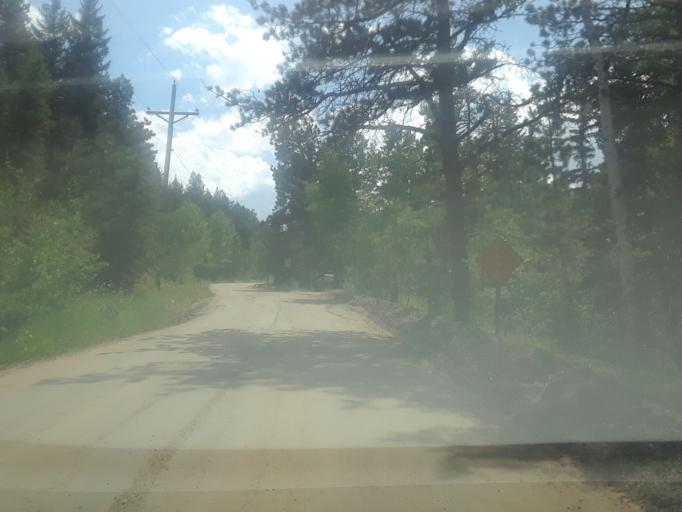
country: US
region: Colorado
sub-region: Boulder County
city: Nederland
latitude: 40.0619
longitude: -105.4140
